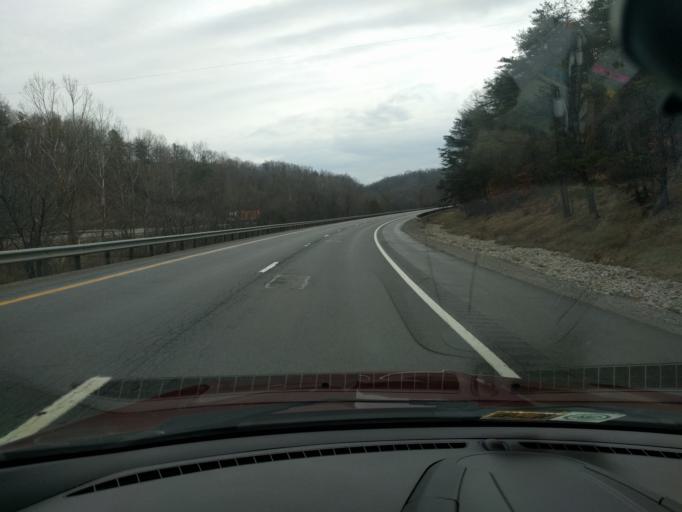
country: US
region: West Virginia
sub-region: Jackson County
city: Ravenswood
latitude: 38.9940
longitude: -81.6652
